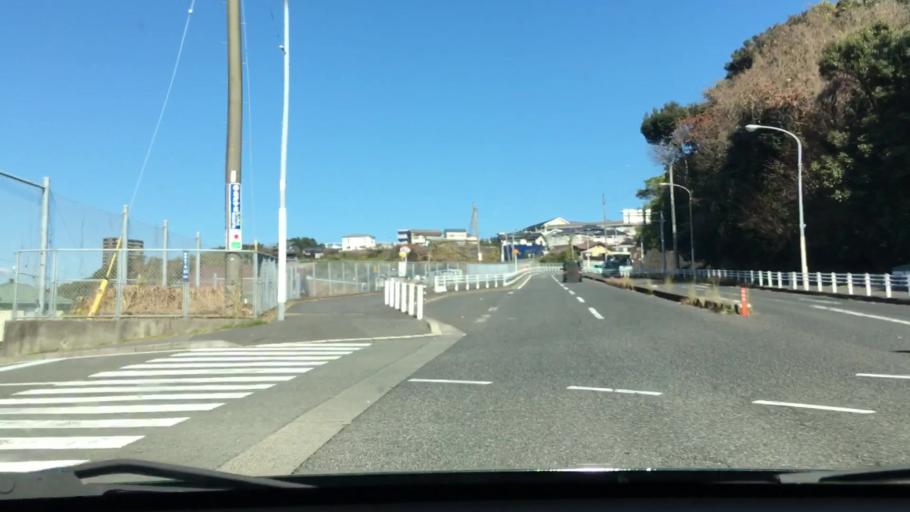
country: JP
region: Kagoshima
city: Kagoshima-shi
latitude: 31.5577
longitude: 130.5261
